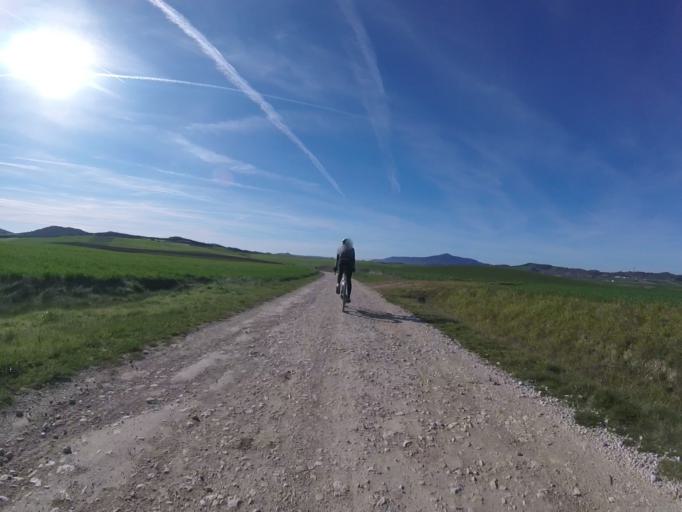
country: ES
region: Navarre
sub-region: Provincia de Navarra
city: Yerri
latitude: 42.7158
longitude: -1.9703
